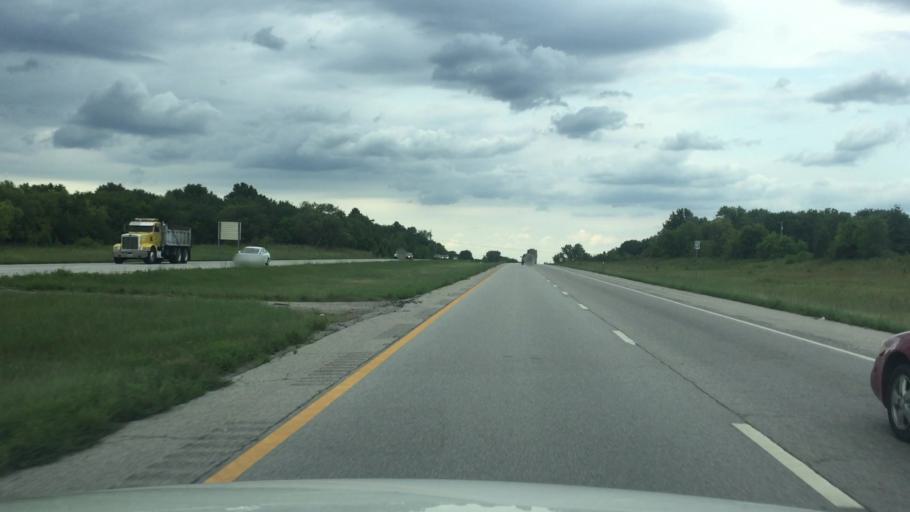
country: US
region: Kansas
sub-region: Johnson County
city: Spring Hill
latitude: 38.7721
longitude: -94.6777
